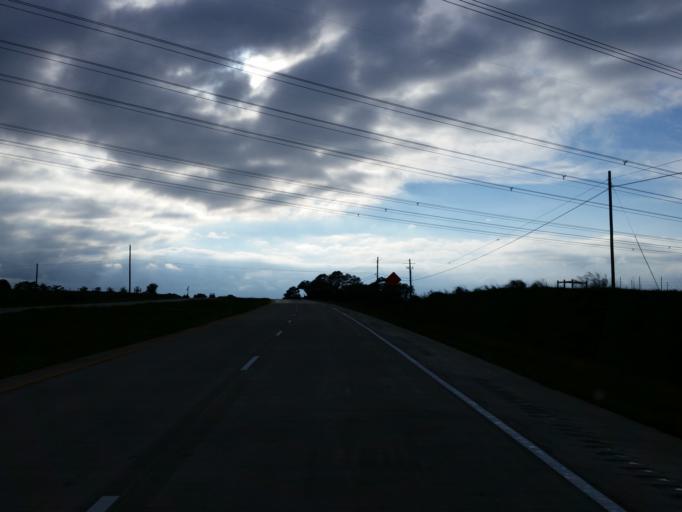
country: US
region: Georgia
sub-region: Bartow County
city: Euharlee
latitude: 34.1081
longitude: -84.9068
